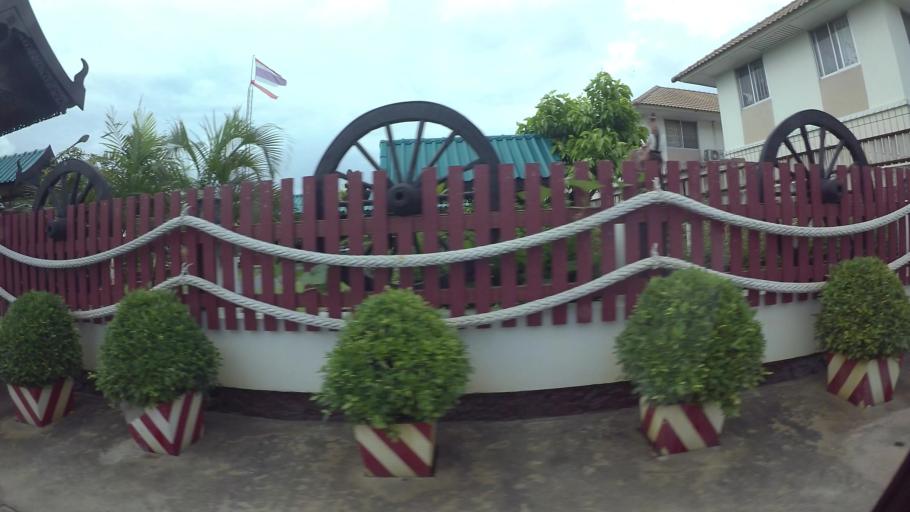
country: TH
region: Chon Buri
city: Si Racha
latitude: 13.1426
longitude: 100.9791
